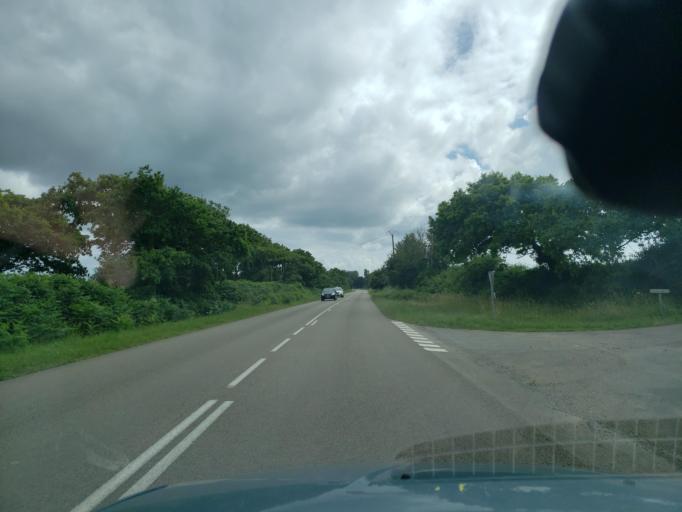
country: FR
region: Brittany
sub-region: Departement du Finistere
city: Ploneour-Lanvern
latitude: 47.8887
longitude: -4.2920
